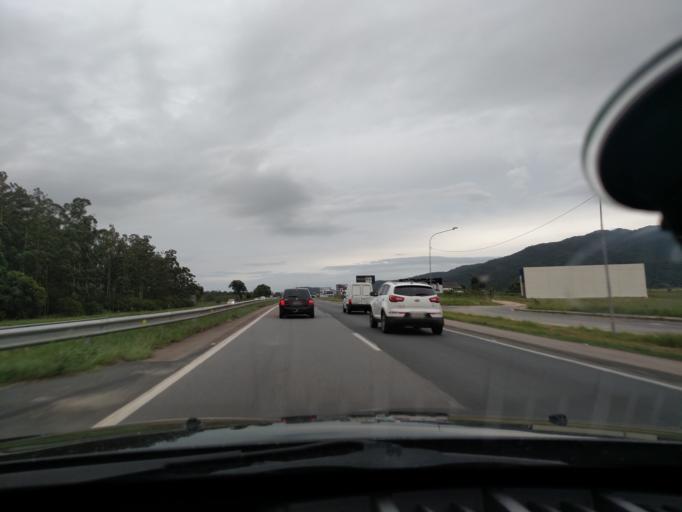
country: BR
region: Santa Catarina
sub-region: Tijucas
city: Tijucas
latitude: -27.2161
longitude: -48.6238
